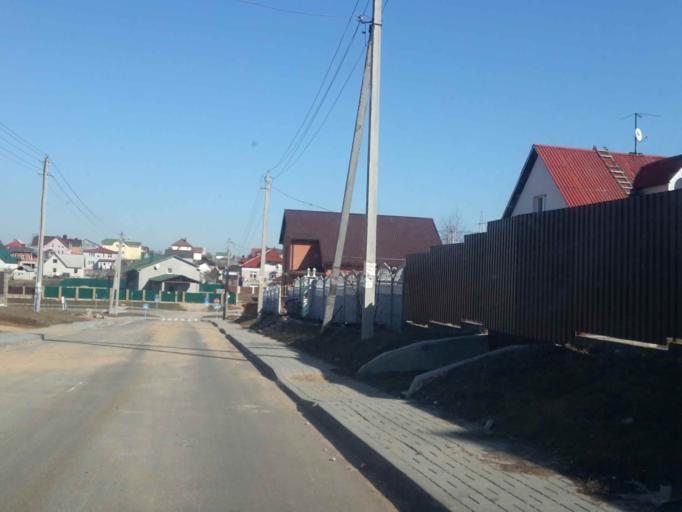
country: BY
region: Minsk
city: Zhdanovichy
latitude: 53.9173
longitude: 27.4088
